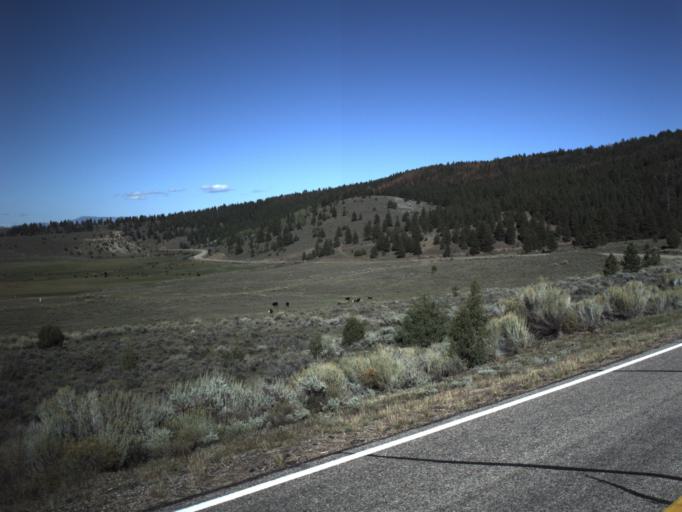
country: US
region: Utah
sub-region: Garfield County
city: Panguitch
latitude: 37.7221
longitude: -112.6195
